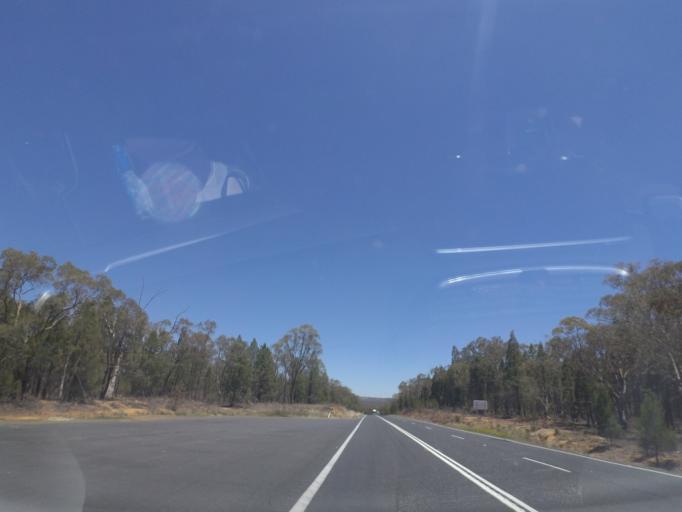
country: AU
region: New South Wales
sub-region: Warrumbungle Shire
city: Coonabarabran
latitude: -31.2344
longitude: 149.3172
